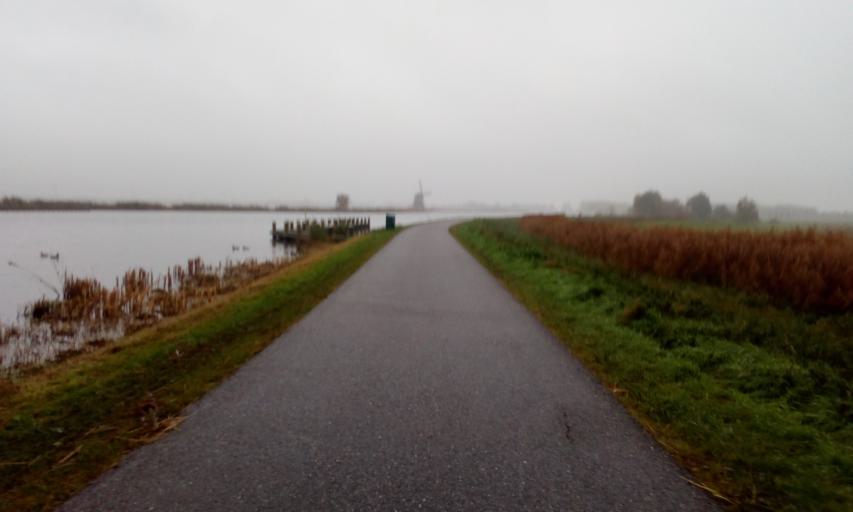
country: NL
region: South Holland
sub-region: Gemeente Lansingerland
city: Bleiswijk
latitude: 52.0264
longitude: 4.5573
